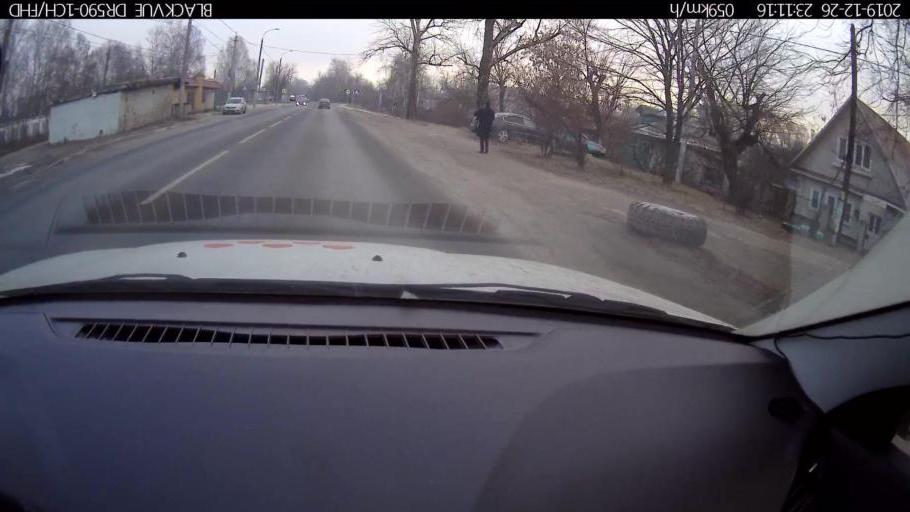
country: RU
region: Nizjnij Novgorod
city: Burevestnik
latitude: 56.2058
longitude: 43.7950
